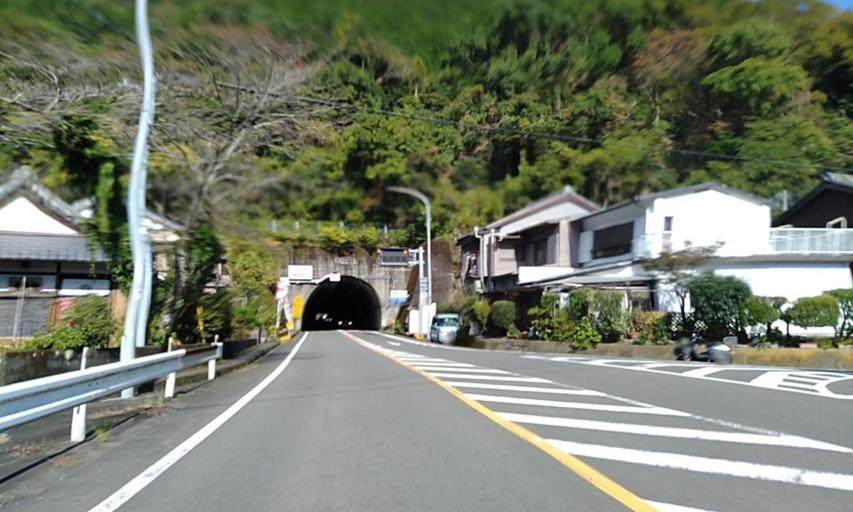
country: JP
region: Mie
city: Owase
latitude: 34.2003
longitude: 136.3281
